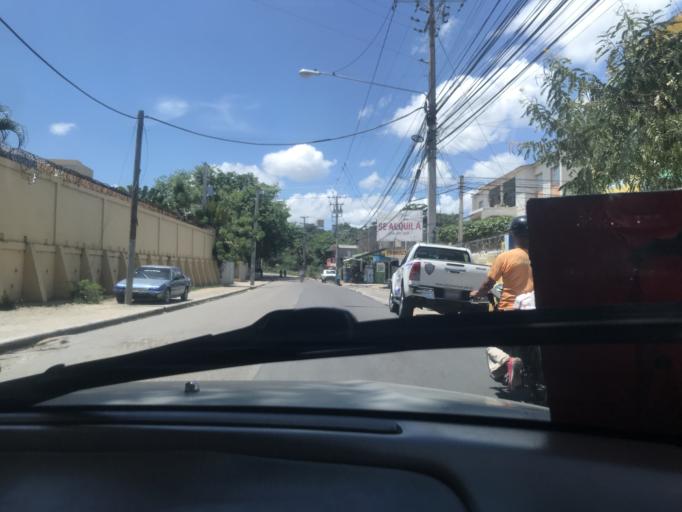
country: DO
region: Santiago
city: Santiago de los Caballeros
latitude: 19.4190
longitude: -70.6892
